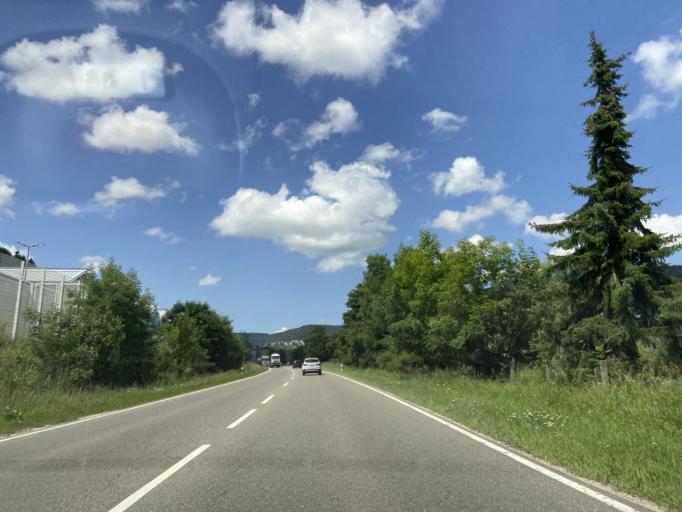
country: DE
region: Baden-Wuerttemberg
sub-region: Tuebingen Region
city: Albstadt
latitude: 48.2023
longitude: 9.0460
